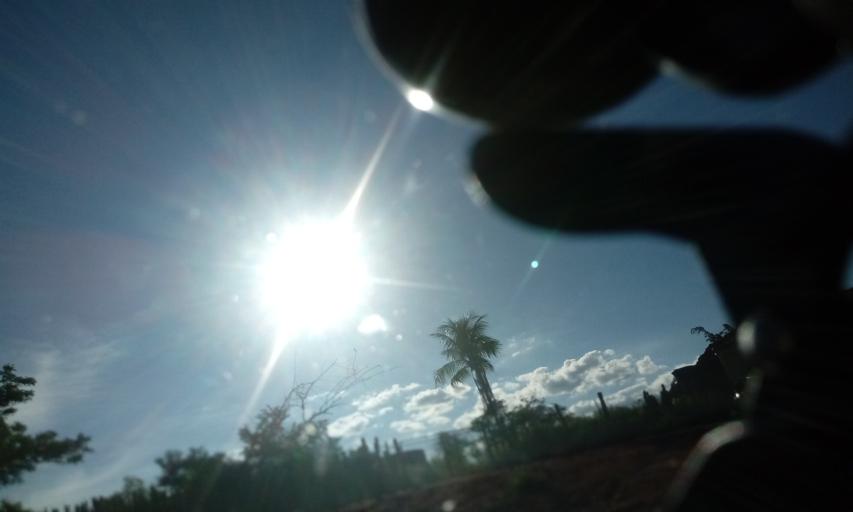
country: BR
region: Bahia
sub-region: Riacho De Santana
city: Riacho de Santana
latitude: -13.8493
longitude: -42.7698
